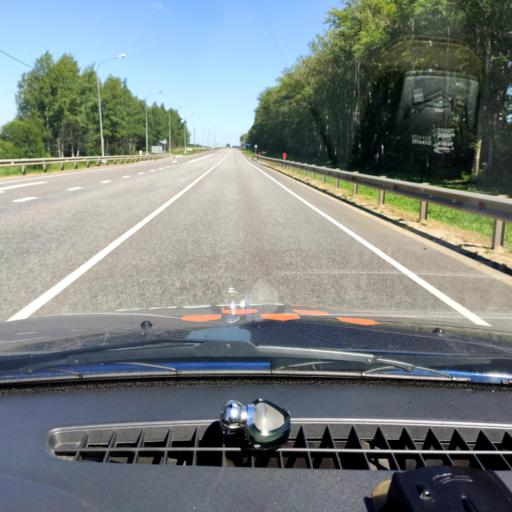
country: RU
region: Orjol
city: Pokrovskoye
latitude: 52.6198
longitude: 36.7503
